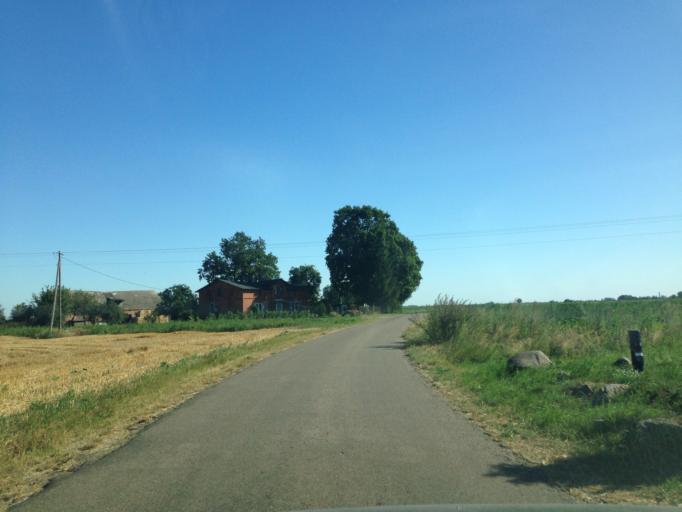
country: PL
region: Kujawsko-Pomorskie
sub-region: Powiat brodnicki
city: Swiedziebnia
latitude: 53.2092
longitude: 19.5223
